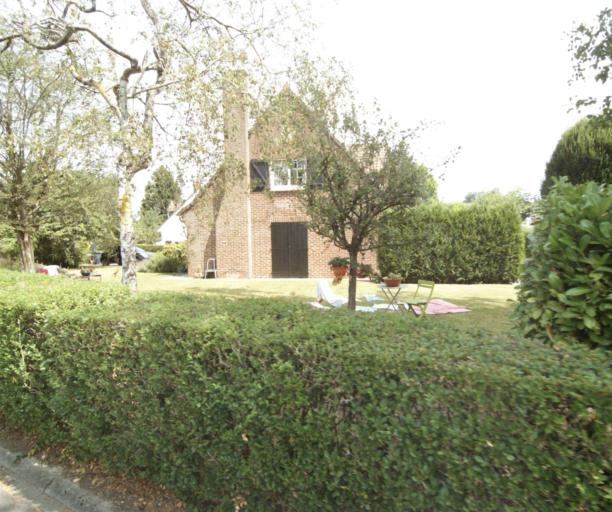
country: FR
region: Nord-Pas-de-Calais
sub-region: Departement du Nord
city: Roncq
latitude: 50.7269
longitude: 3.1198
